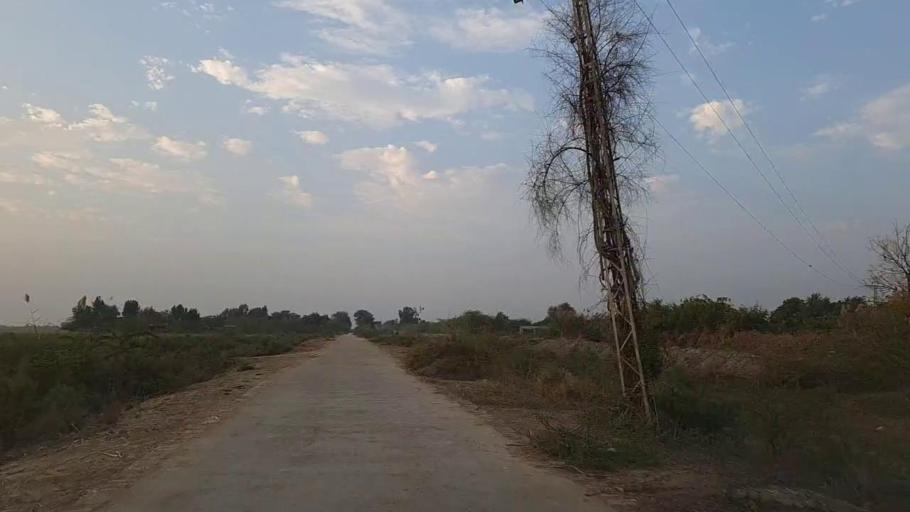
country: PK
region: Sindh
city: Mirwah Gorchani
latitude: 25.3394
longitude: 69.2080
